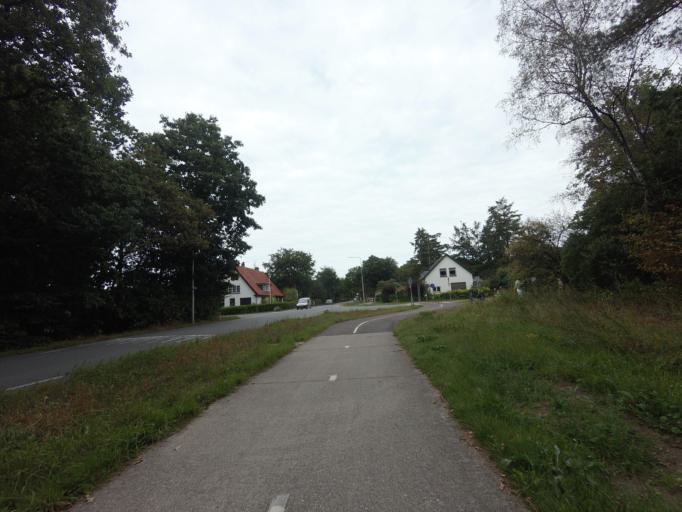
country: NL
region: Gelderland
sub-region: Gemeente Arnhem
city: Hoogkamp
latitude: 52.0344
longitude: 5.8874
